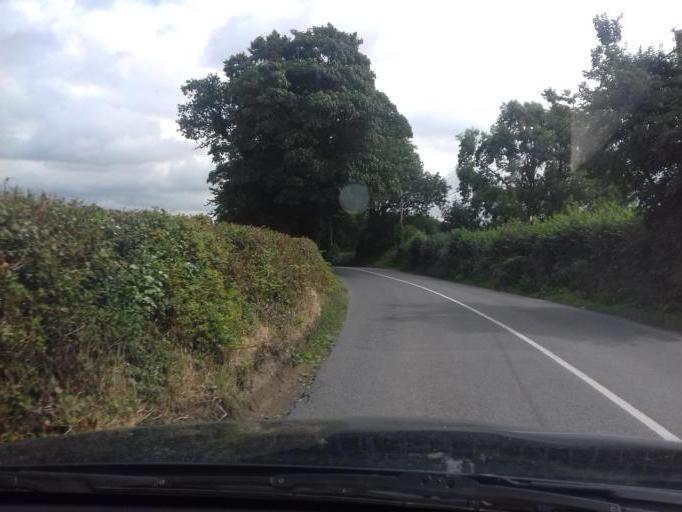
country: IE
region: Leinster
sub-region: Loch Garman
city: Enniscorthy
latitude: 52.4893
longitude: -6.4990
